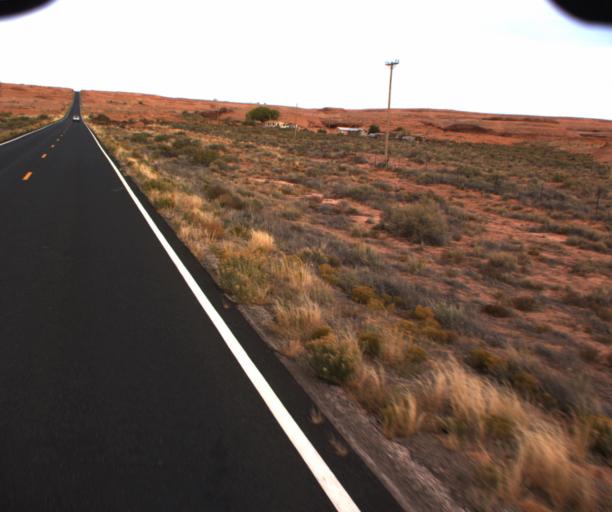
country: US
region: Arizona
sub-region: Apache County
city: Many Farms
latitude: 36.7781
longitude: -109.6594
